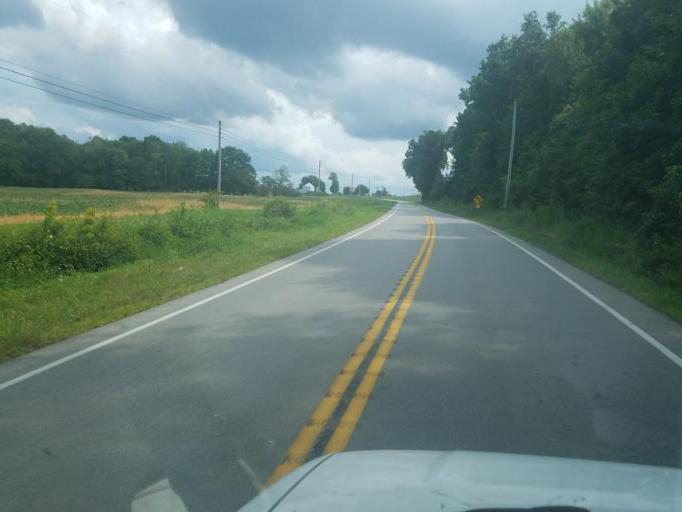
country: US
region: Pennsylvania
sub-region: Crawford County
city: Conneaut Lakeshore
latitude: 41.5874
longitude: -80.3030
